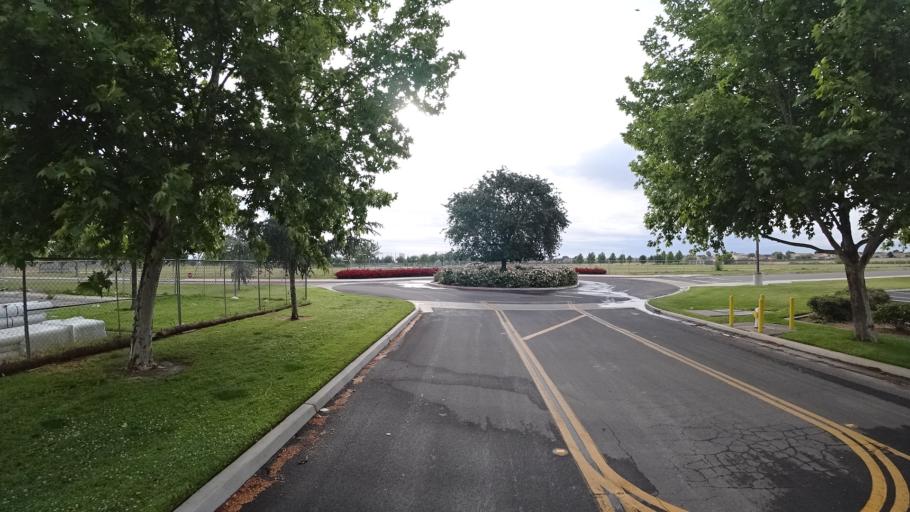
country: US
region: California
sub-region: Kings County
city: Armona
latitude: 36.3350
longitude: -119.6876
